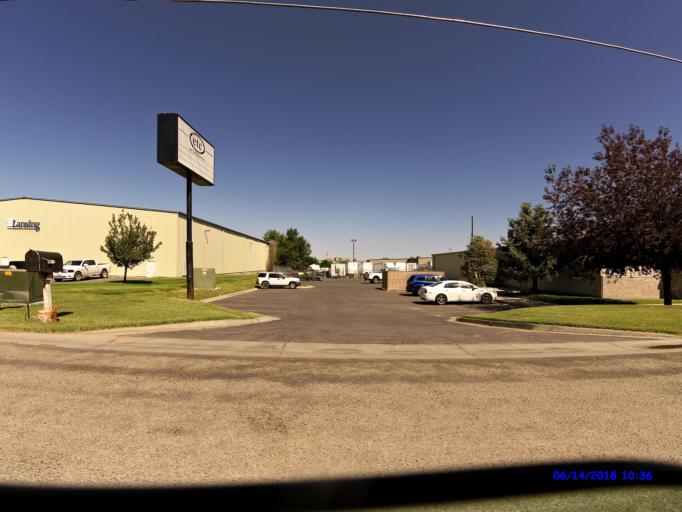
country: US
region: Utah
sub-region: Weber County
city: West Haven
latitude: 41.2116
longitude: -112.0156
